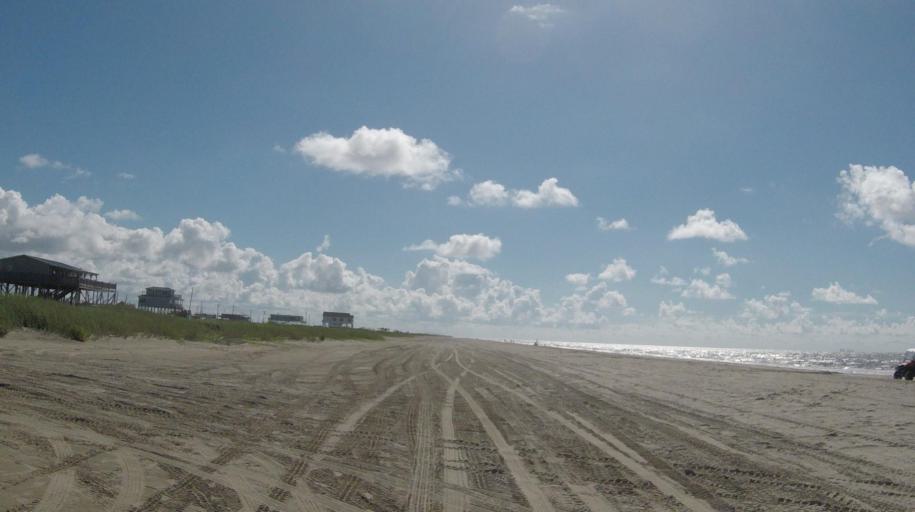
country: US
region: Louisiana
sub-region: Cameron Parish
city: Cameron
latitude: 29.7694
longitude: -93.4517
